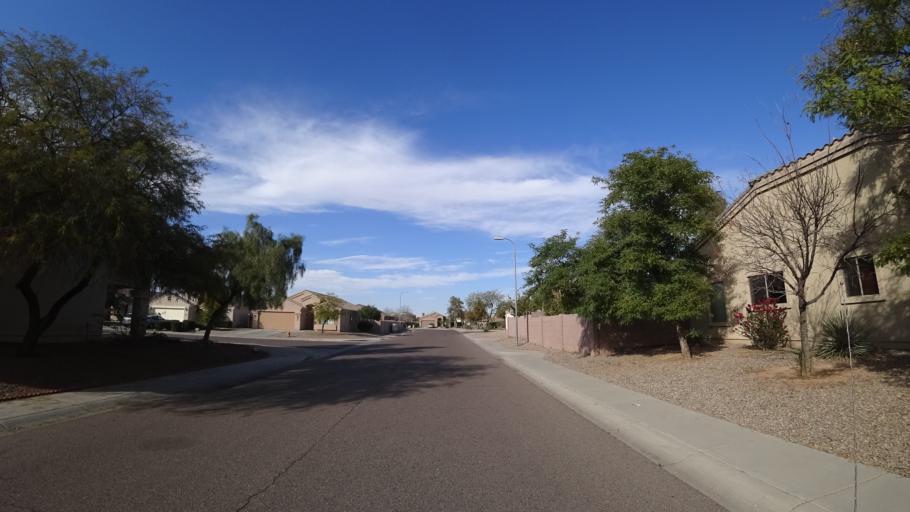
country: US
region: Arizona
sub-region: Maricopa County
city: Tolleson
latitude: 33.4295
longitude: -112.2878
